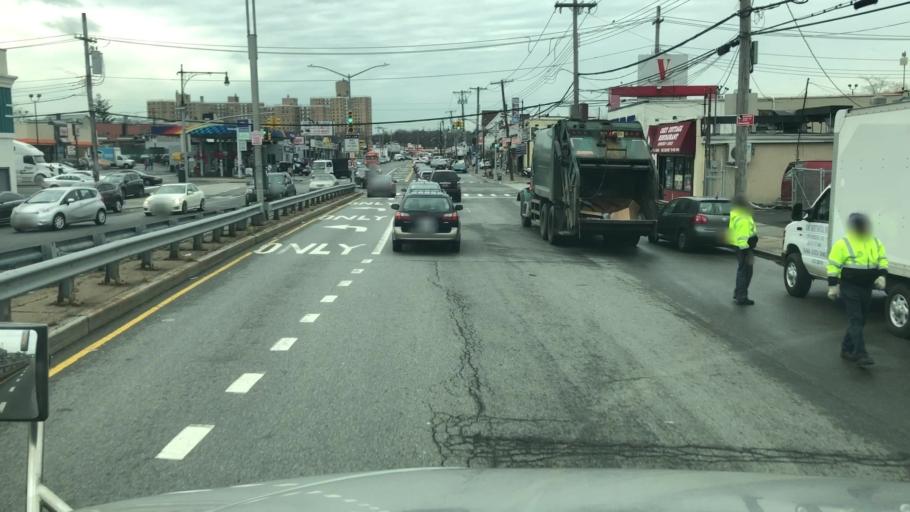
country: US
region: New York
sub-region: Bronx
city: Eastchester
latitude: 40.8863
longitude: -73.8272
